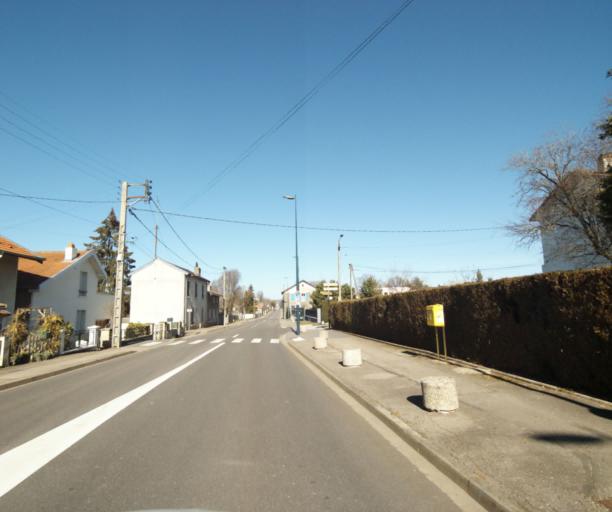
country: FR
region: Lorraine
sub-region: Departement de Meurthe-et-Moselle
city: Heillecourt
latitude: 48.6594
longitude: 6.2066
